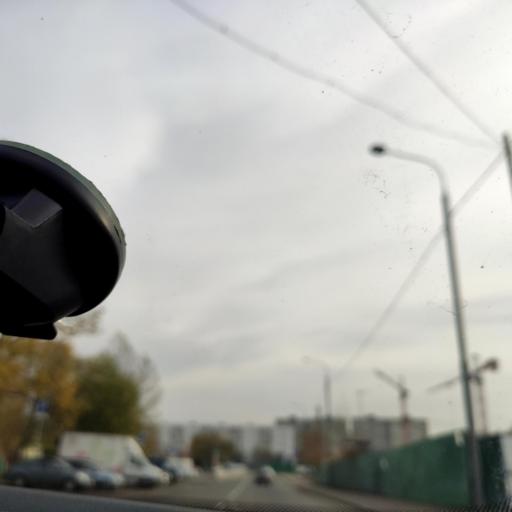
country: RU
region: Moskovskaya
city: Vostochnoe Degunino
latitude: 55.8873
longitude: 37.5510
